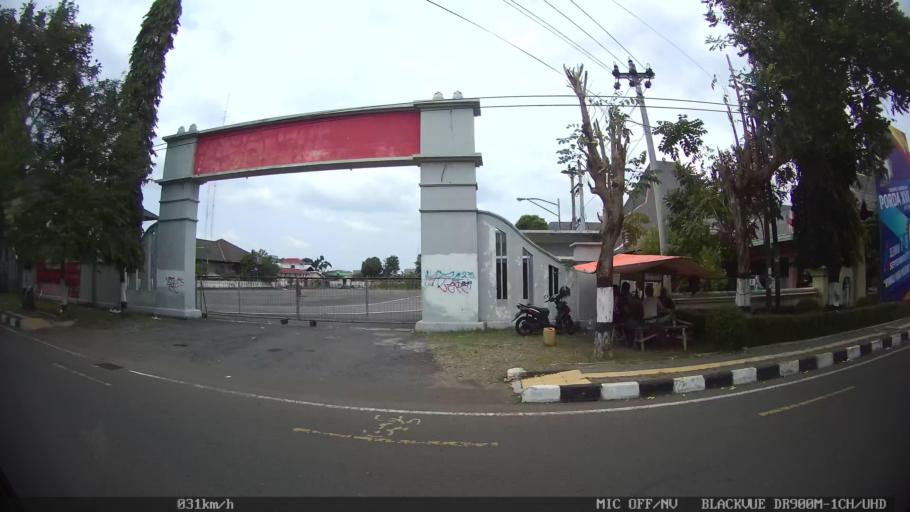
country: ID
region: Daerah Istimewa Yogyakarta
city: Yogyakarta
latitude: -7.7981
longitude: 110.3864
